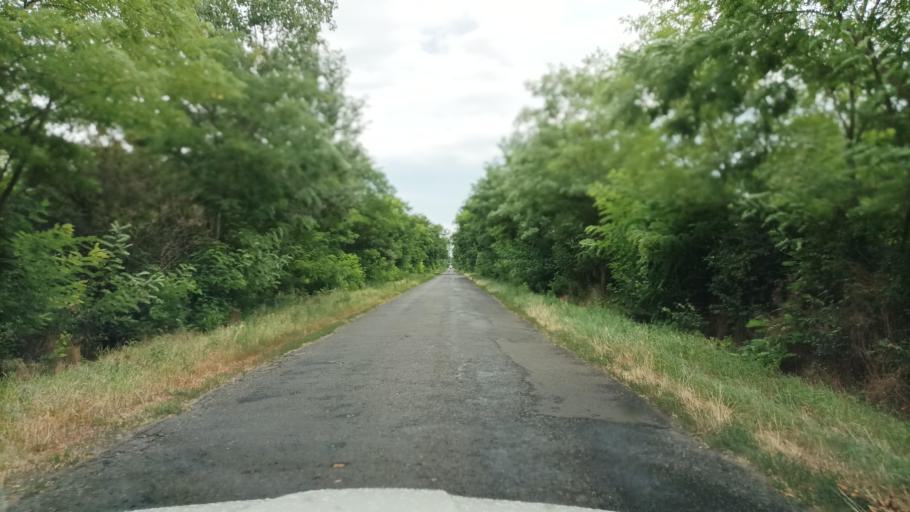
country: HU
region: Pest
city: Orkeny
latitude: 47.0482
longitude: 19.3352
